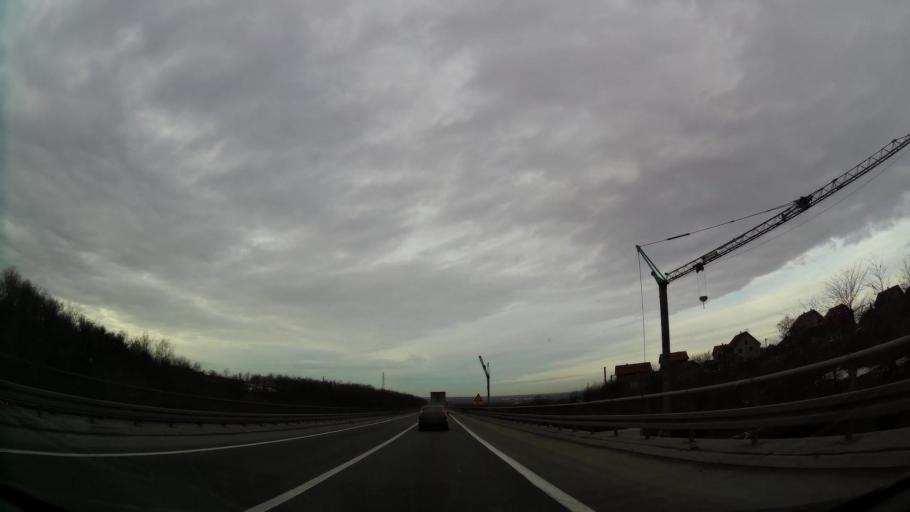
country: RS
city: Ostruznica
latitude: 44.7175
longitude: 20.3606
